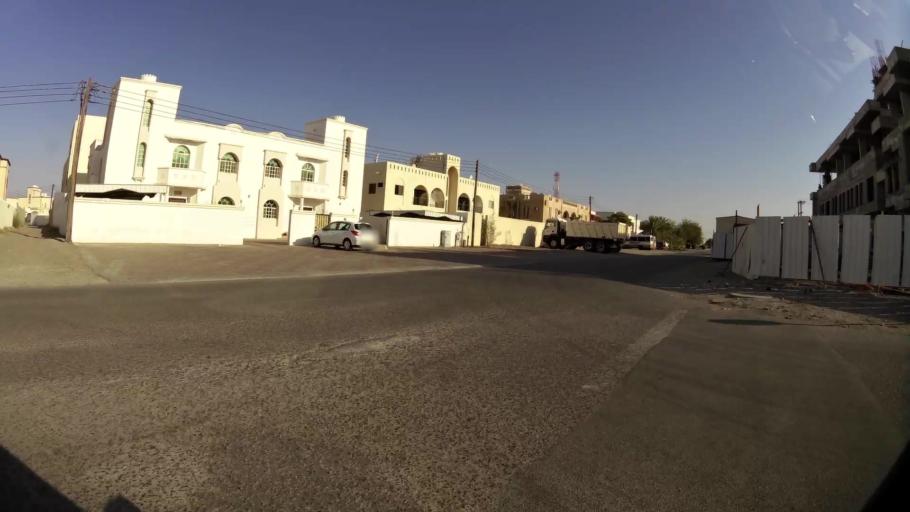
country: OM
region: Muhafazat Masqat
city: As Sib al Jadidah
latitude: 23.6349
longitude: 58.2038
